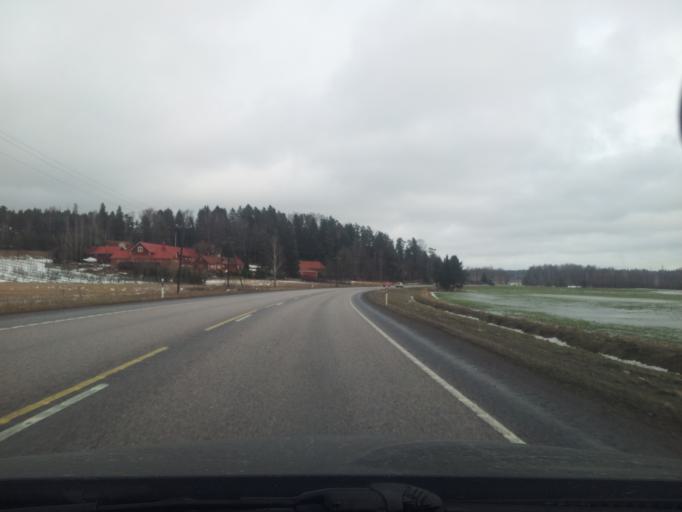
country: FI
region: Uusimaa
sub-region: Helsinki
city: Espoo
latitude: 60.1819
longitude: 24.5605
